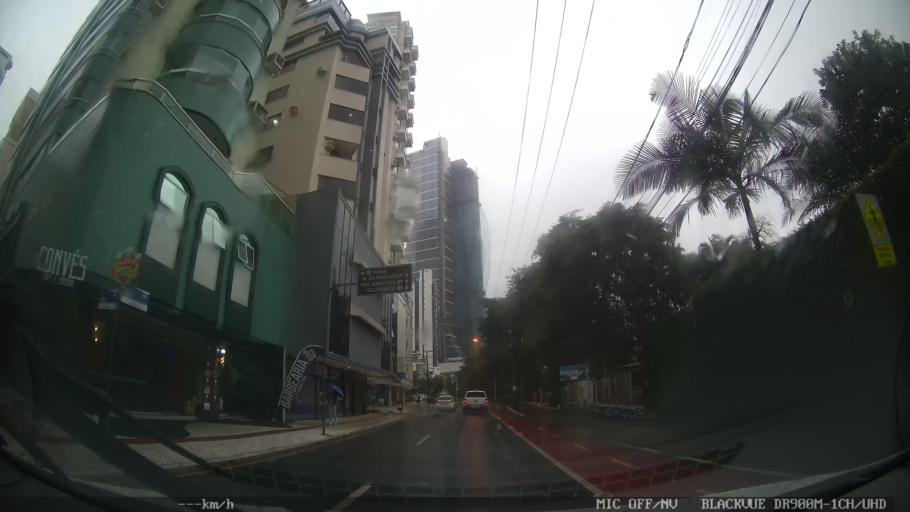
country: BR
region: Santa Catarina
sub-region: Balneario Camboriu
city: Balneario Camboriu
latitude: -27.0047
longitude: -48.6196
